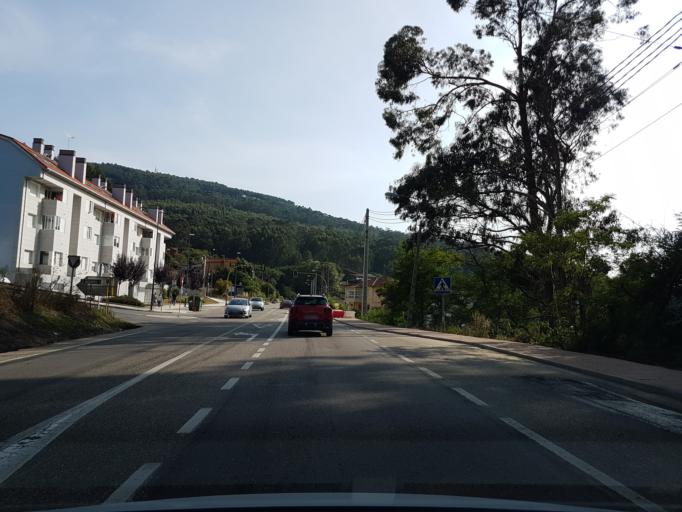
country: ES
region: Galicia
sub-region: Provincia de Pontevedra
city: Nigran
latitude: 42.1857
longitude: -8.7874
